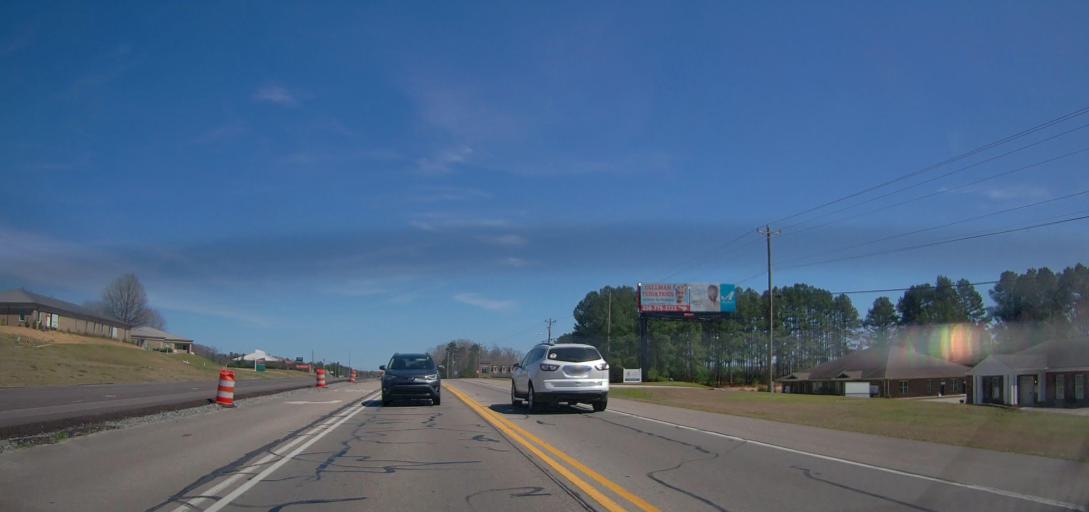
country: US
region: Alabama
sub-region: Cullman County
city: Cullman
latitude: 34.1986
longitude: -86.8070
